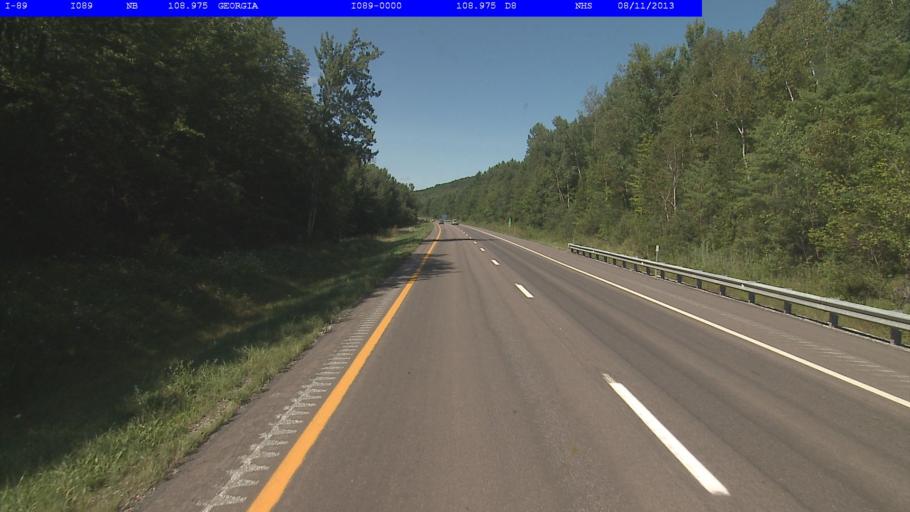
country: US
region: Vermont
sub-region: Franklin County
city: Saint Albans
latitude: 44.7265
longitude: -73.0810
